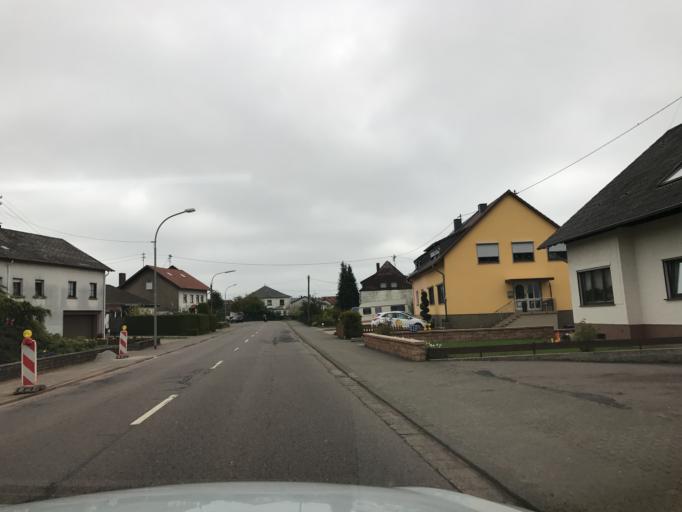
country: DE
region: Saarland
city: Orscholz
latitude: 49.5052
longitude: 6.5192
